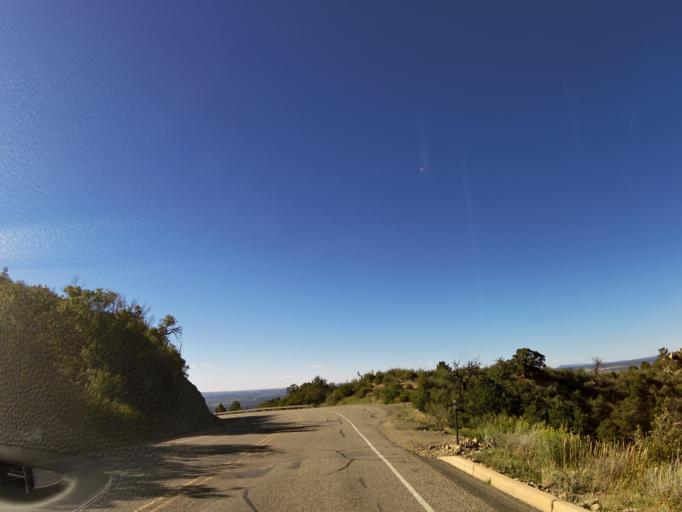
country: US
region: Colorado
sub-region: Montezuma County
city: Mancos
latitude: 37.3190
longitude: -108.4167
